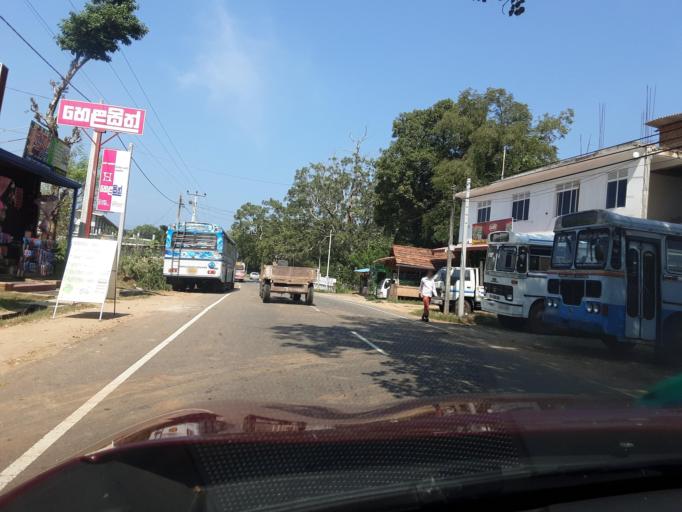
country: LK
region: Uva
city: Badulla
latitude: 7.1855
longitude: 81.0418
